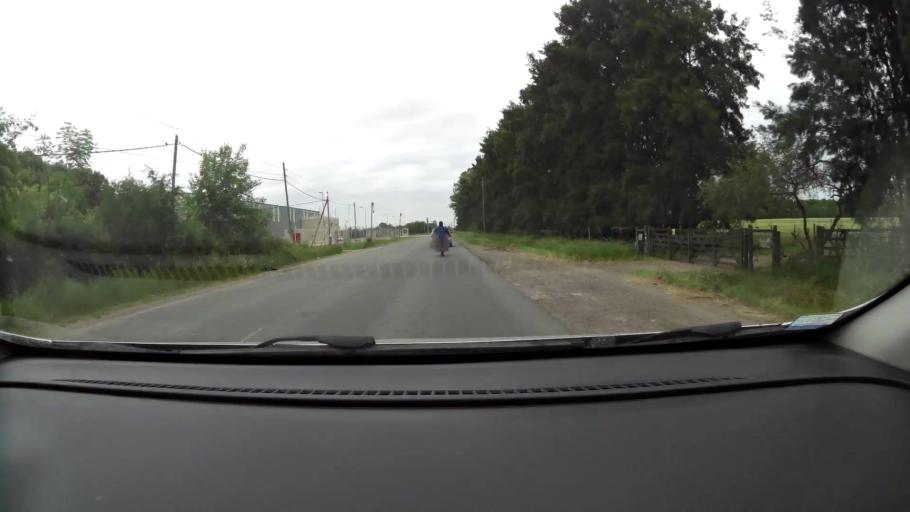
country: AR
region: Buenos Aires
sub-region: Partido de Zarate
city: Zarate
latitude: -34.1007
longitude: -59.0894
